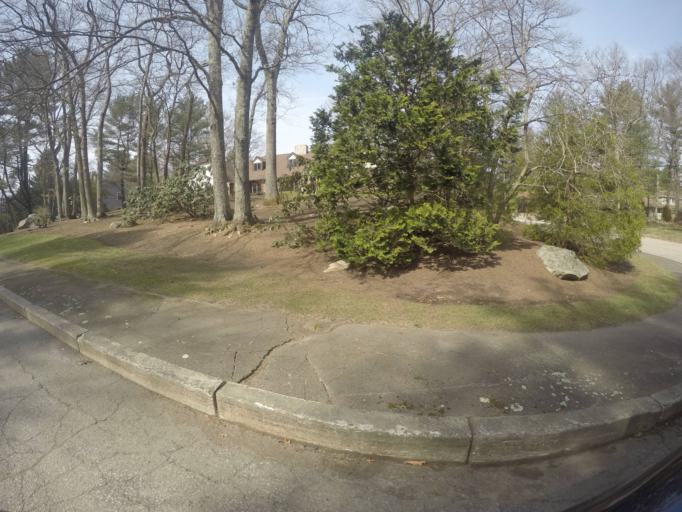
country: US
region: Massachusetts
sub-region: Bristol County
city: Easton
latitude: 42.0514
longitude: -71.1221
